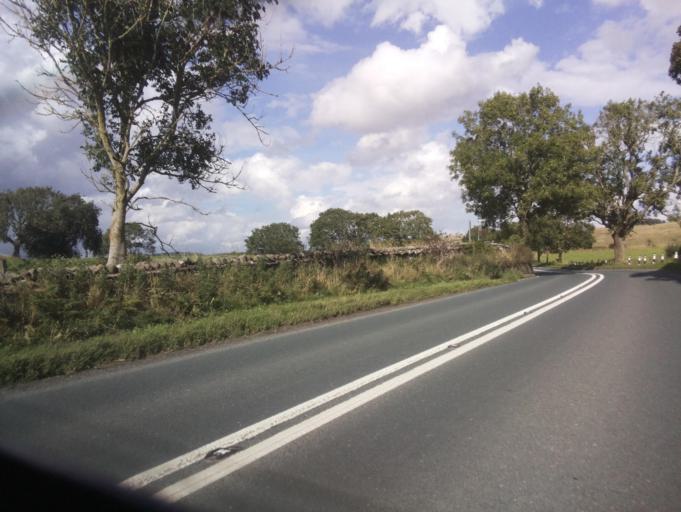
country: GB
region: England
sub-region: North Yorkshire
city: Leyburn
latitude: 54.3467
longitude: -1.8112
